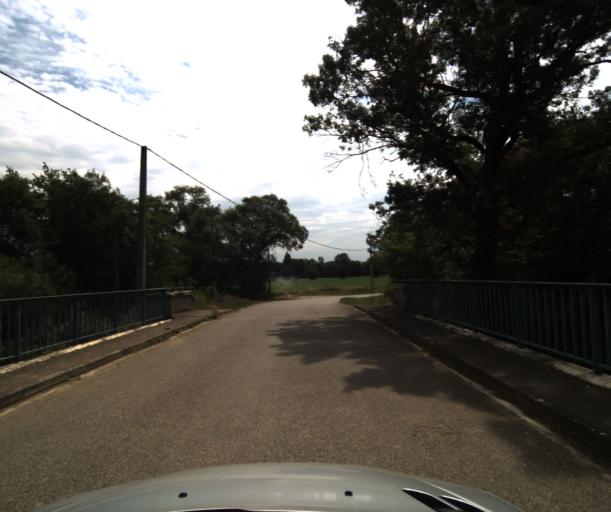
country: FR
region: Midi-Pyrenees
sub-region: Departement de la Haute-Garonne
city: Lacasse
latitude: 43.4128
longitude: 1.2803
